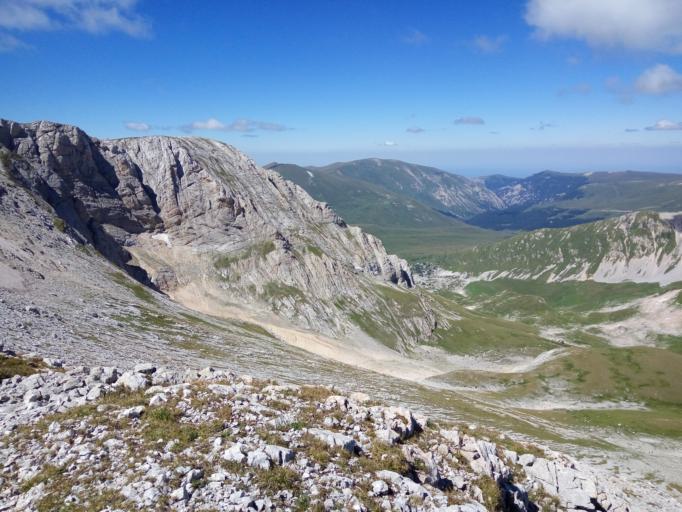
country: RU
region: Krasnodarskiy
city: Dagomys
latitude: 43.9812
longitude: 39.9040
